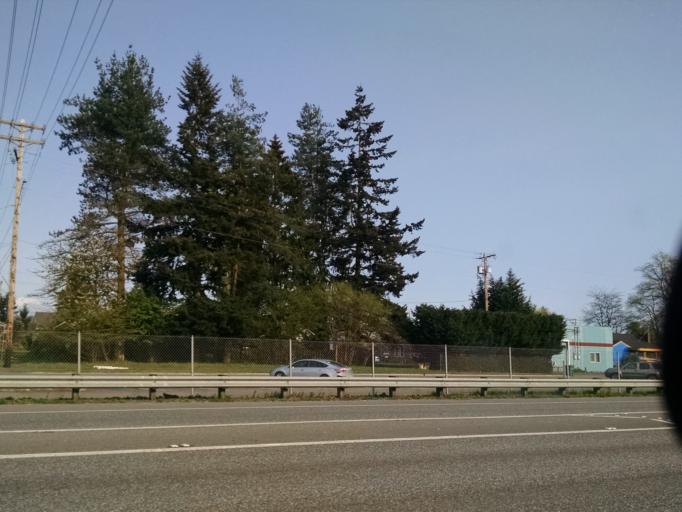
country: US
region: Washington
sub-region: Snohomish County
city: Marysville
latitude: 48.0555
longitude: -122.1845
